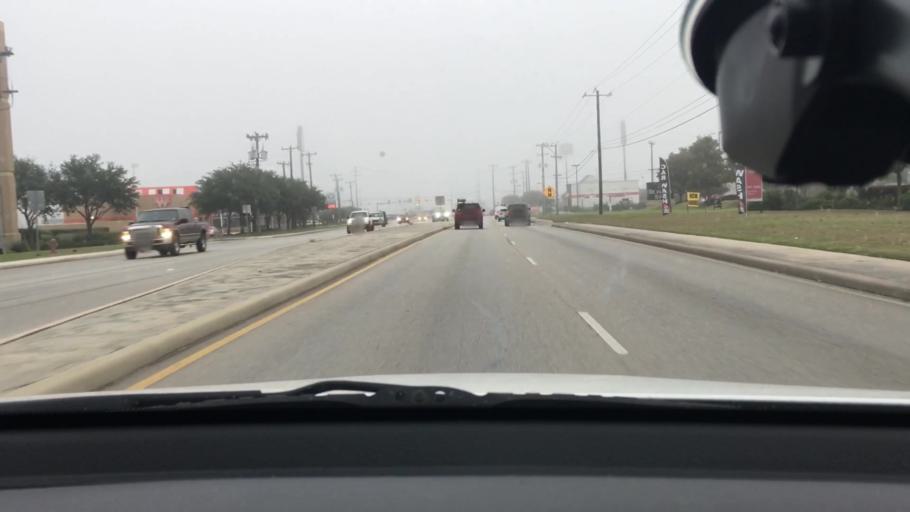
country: US
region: Texas
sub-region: Bexar County
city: Selma
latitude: 29.6028
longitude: -98.2789
